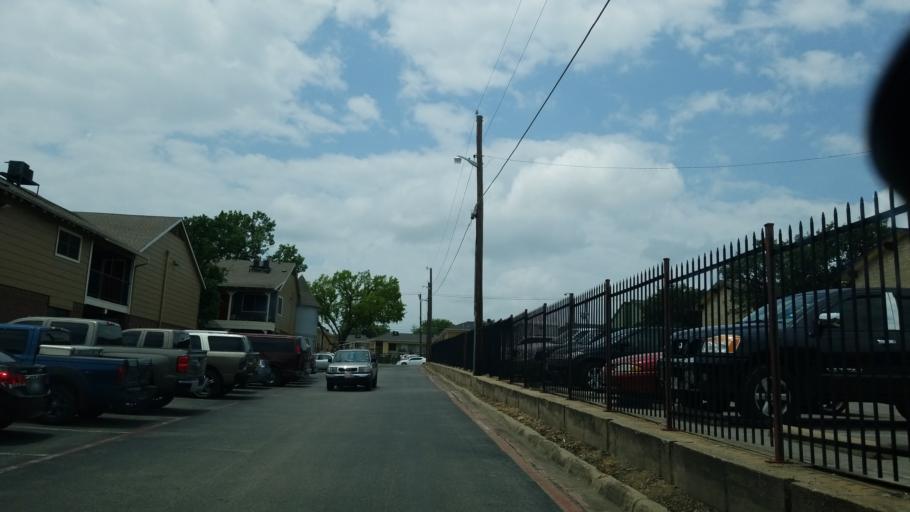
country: US
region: Texas
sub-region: Dallas County
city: Farmers Branch
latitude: 32.8731
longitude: -96.8669
